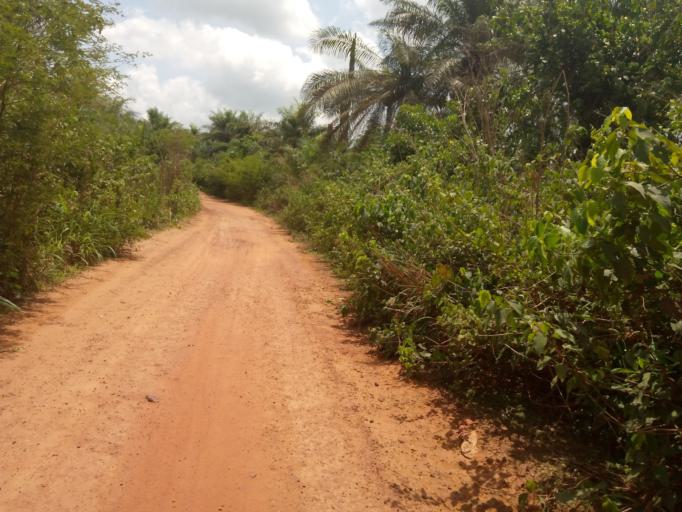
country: SL
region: Western Area
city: Waterloo
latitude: 8.3765
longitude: -12.9651
